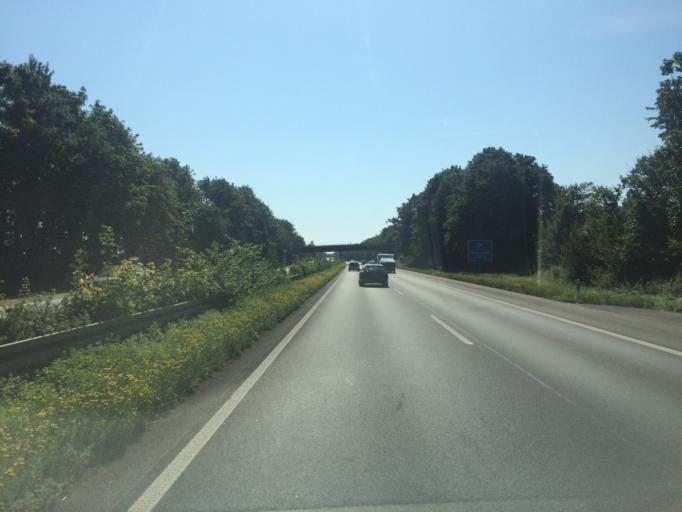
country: DE
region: North Rhine-Westphalia
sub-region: Regierungsbezirk Munster
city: Ascheberg
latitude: 51.7615
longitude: 7.6424
